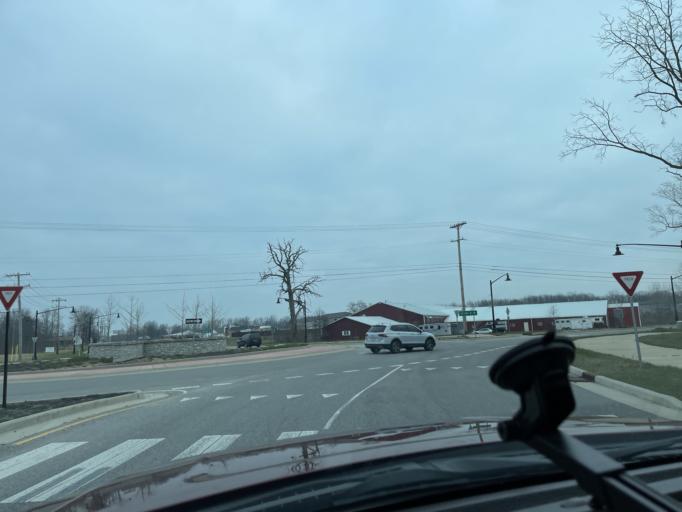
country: US
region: Indiana
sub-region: Hendricks County
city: Fairfield Heights
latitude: 39.8064
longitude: -86.4007
